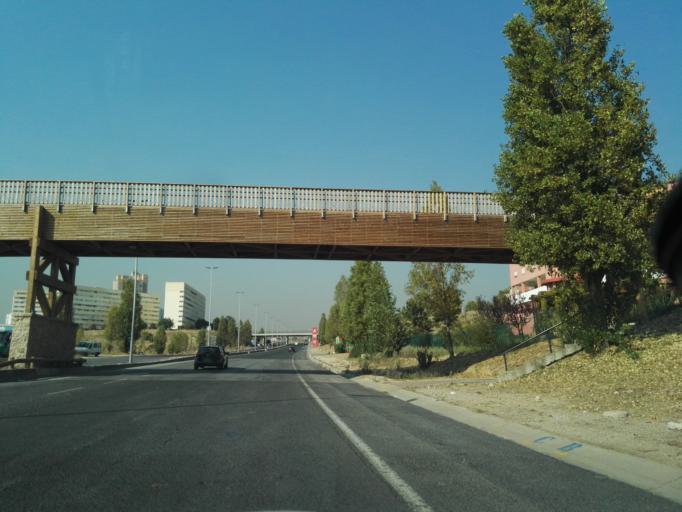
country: PT
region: Lisbon
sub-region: Loures
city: Moscavide
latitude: 38.7525
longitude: -9.1186
